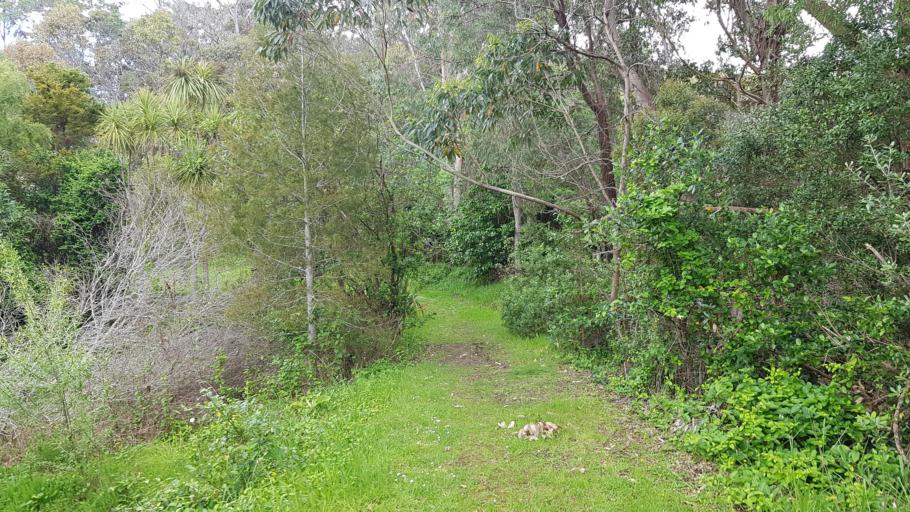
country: NZ
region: Auckland
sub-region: Auckland
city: Pakuranga
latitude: -36.7750
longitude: 175.0062
